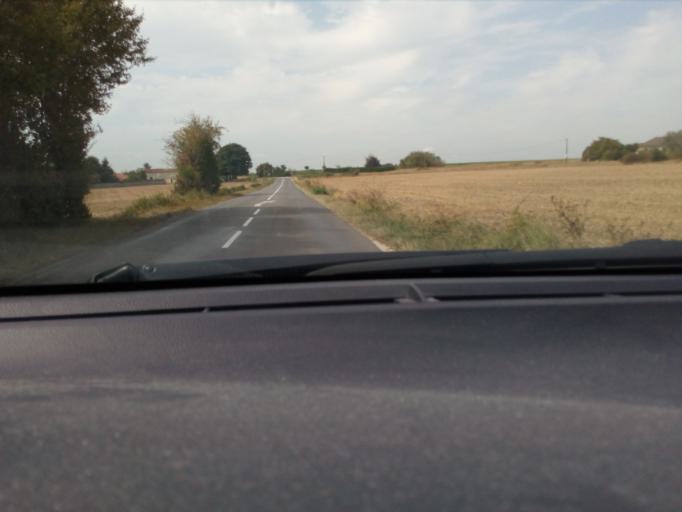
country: FR
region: Poitou-Charentes
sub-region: Departement de la Charente
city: Saint-Saturnin
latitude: 45.6691
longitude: 0.0283
